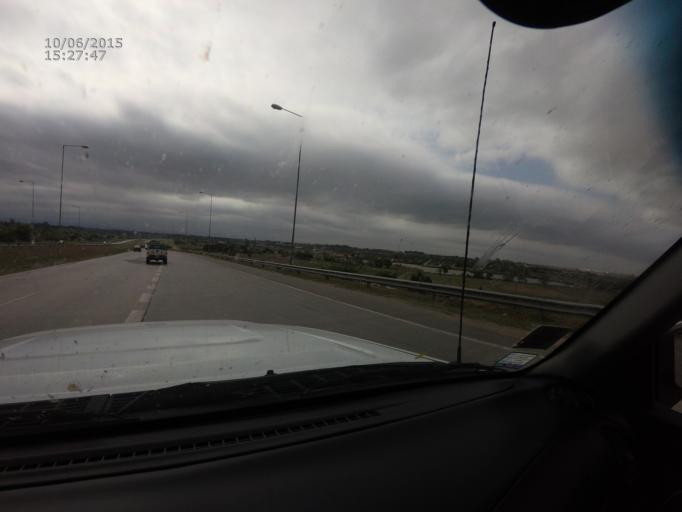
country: AR
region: Cordoba
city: Malvinas Argentinas
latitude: -31.4171
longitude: -64.1126
